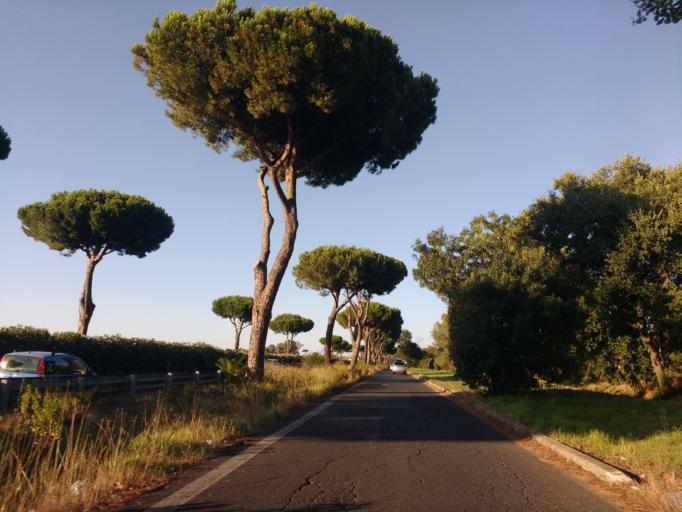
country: IT
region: Latium
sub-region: Citta metropolitana di Roma Capitale
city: Acilia-Castel Fusano-Ostia Antica
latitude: 41.7576
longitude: 12.3737
